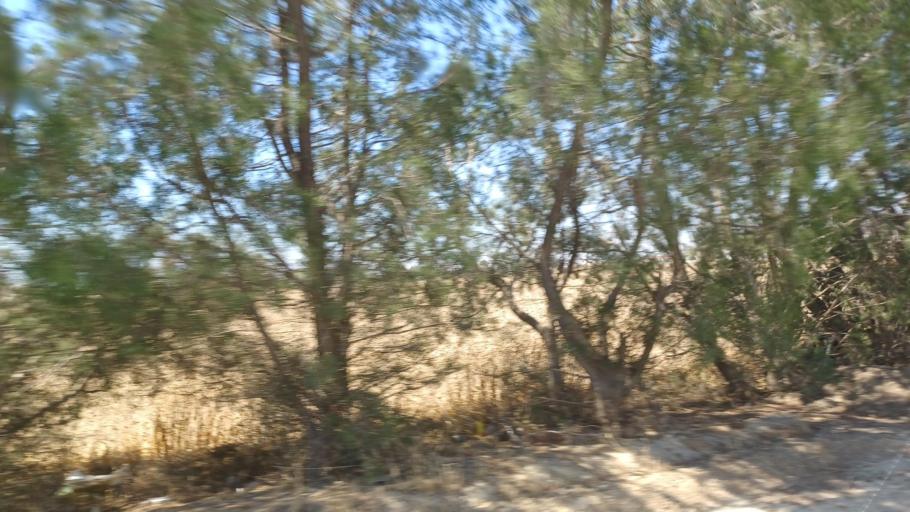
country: CY
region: Larnaka
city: Voroklini
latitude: 34.9949
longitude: 33.6677
